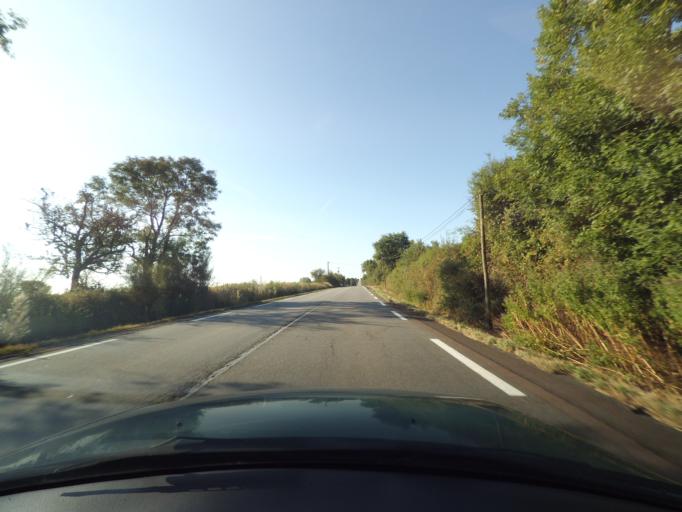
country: FR
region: Poitou-Charentes
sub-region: Departement des Deux-Sevres
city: Chiche
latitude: 46.7650
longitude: -0.3133
